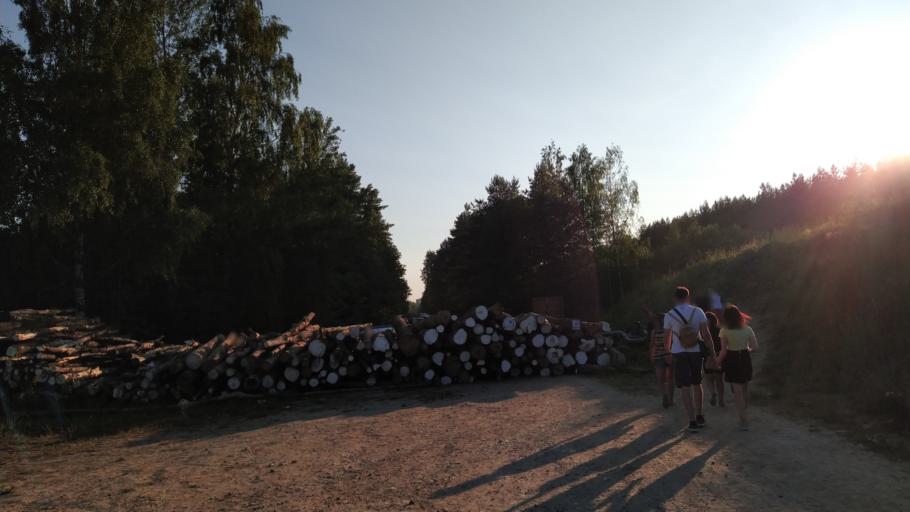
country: RU
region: Leningrad
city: Toksovo
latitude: 60.1136
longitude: 30.5197
